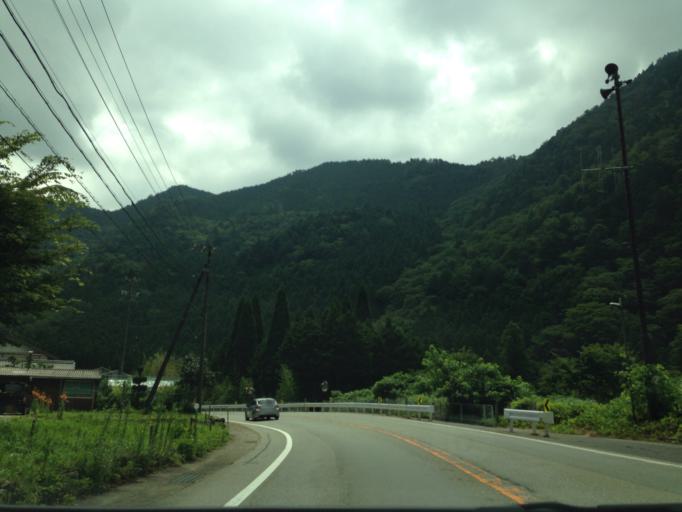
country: JP
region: Gifu
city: Gujo
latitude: 35.7492
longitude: 137.2151
